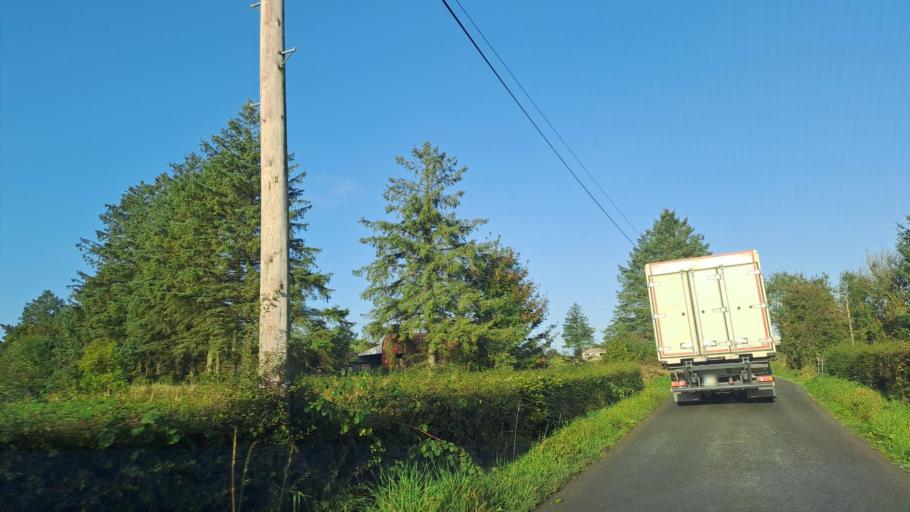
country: IE
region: Ulster
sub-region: County Monaghan
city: Castleblayney
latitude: 54.0763
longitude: -6.8407
